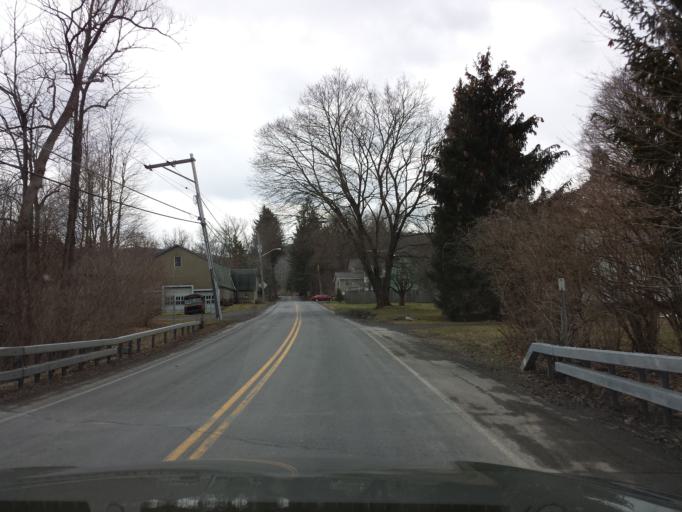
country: US
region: New York
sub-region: Tompkins County
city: Dryden
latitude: 42.3931
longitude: -76.3450
